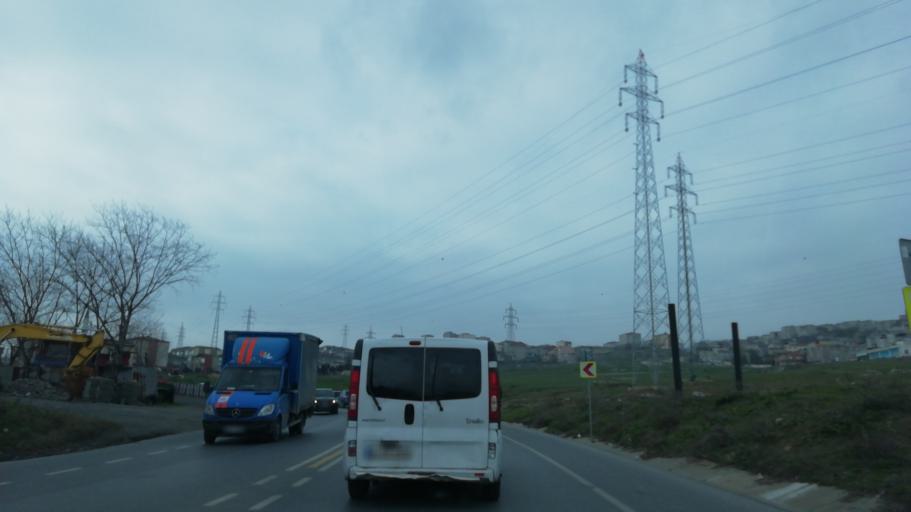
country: TR
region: Istanbul
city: Esenyurt
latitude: 41.0629
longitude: 28.7381
